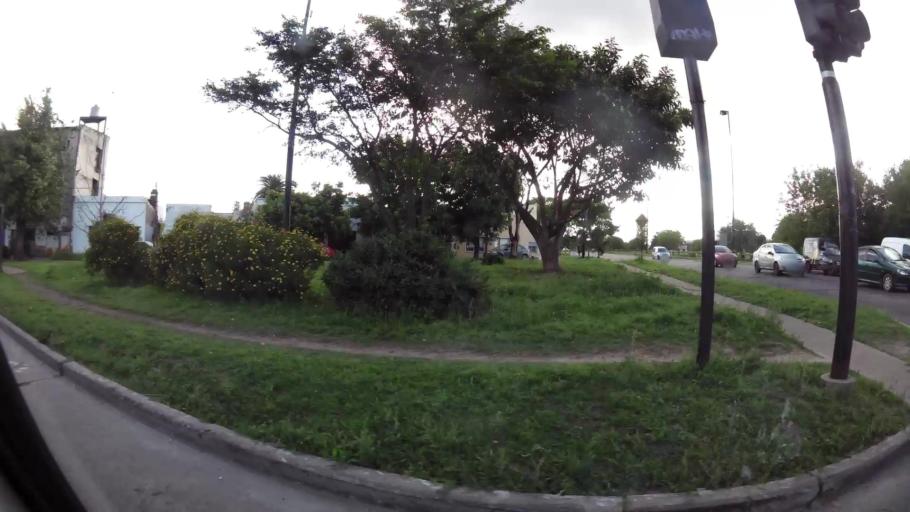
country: AR
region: Buenos Aires
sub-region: Partido de La Plata
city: La Plata
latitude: -34.8925
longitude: -57.9565
